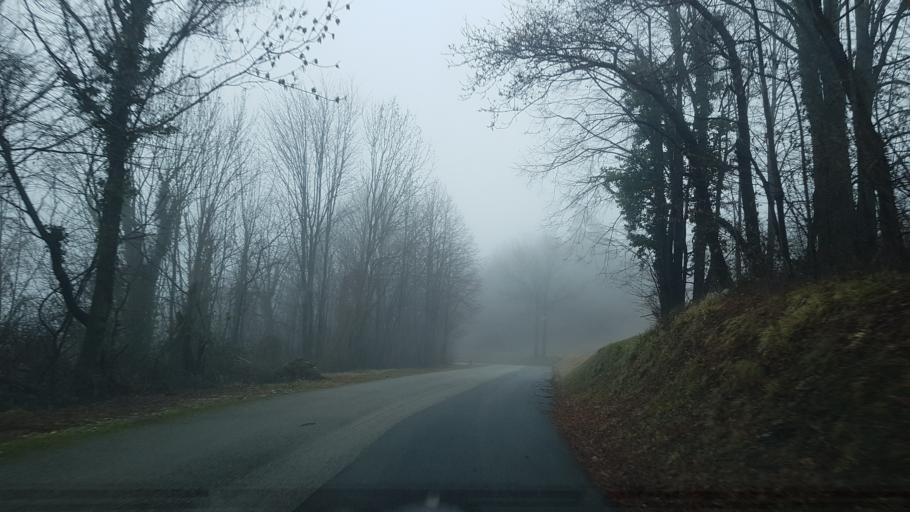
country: IT
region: Friuli Venezia Giulia
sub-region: Provincia di Udine
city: Stregna
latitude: 46.1176
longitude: 13.5860
